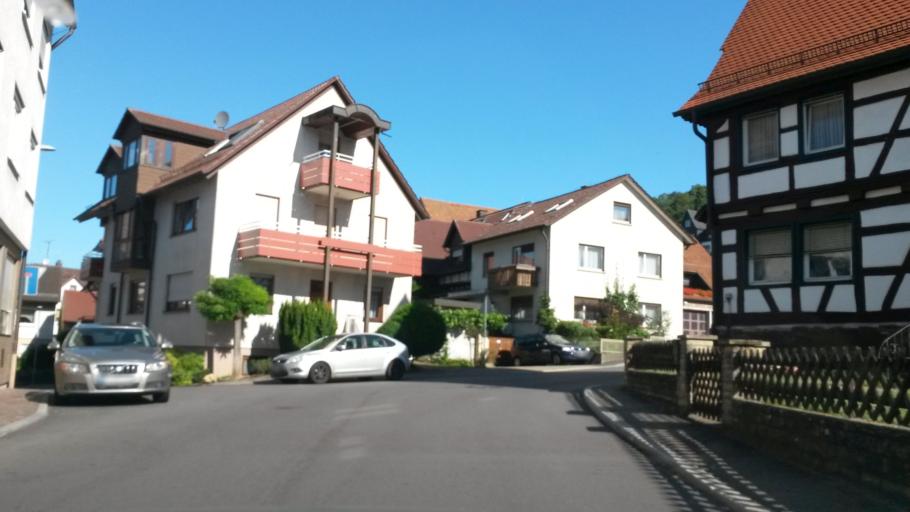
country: DE
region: Baden-Wuerttemberg
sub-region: Karlsruhe Region
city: Eisingen
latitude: 48.9336
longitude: 8.6344
